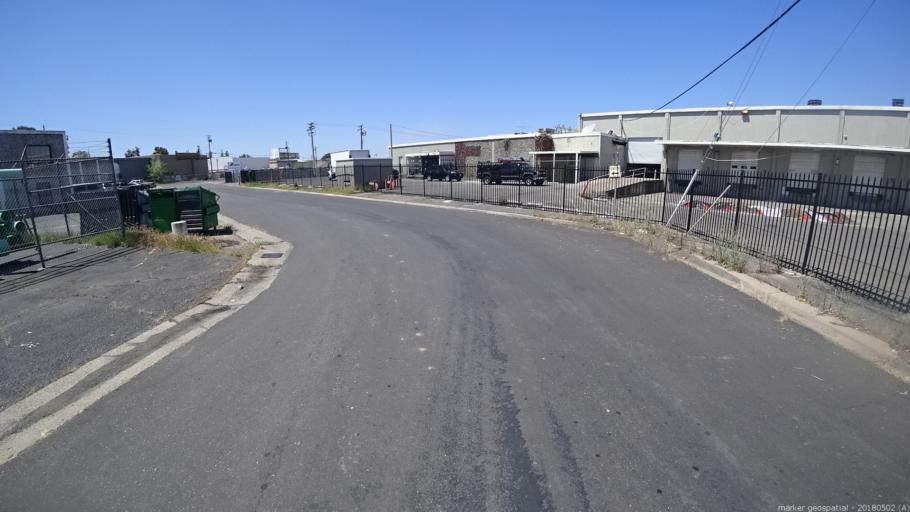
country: US
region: California
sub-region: Sacramento County
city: Sacramento
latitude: 38.6020
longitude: -121.4427
